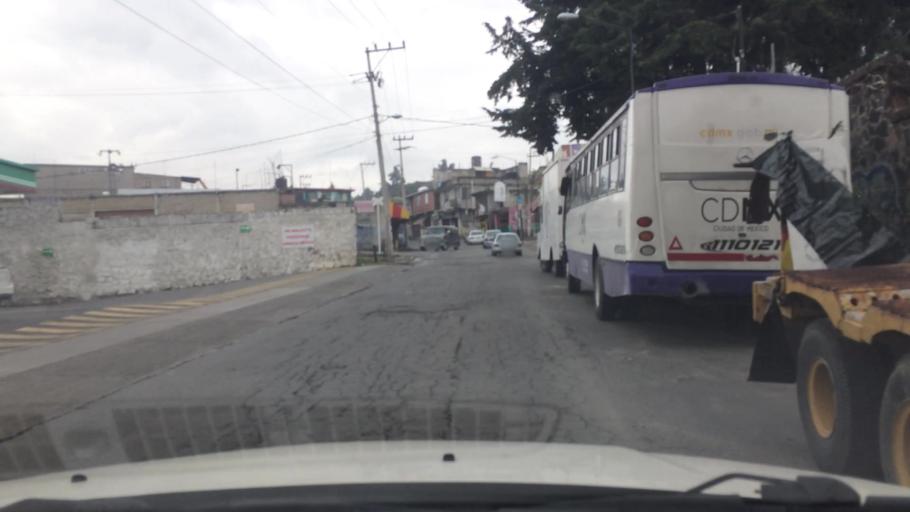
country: MX
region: Mexico City
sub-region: Tlalpan
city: Lomas de Tepemecatl
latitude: 19.2291
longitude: -99.1971
